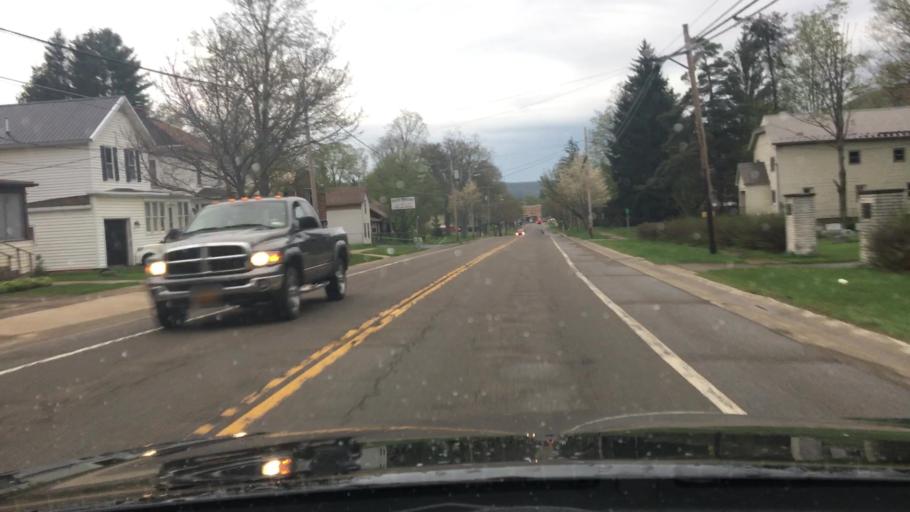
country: US
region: New York
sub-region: Cattaraugus County
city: Little Valley
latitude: 42.2520
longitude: -78.8038
